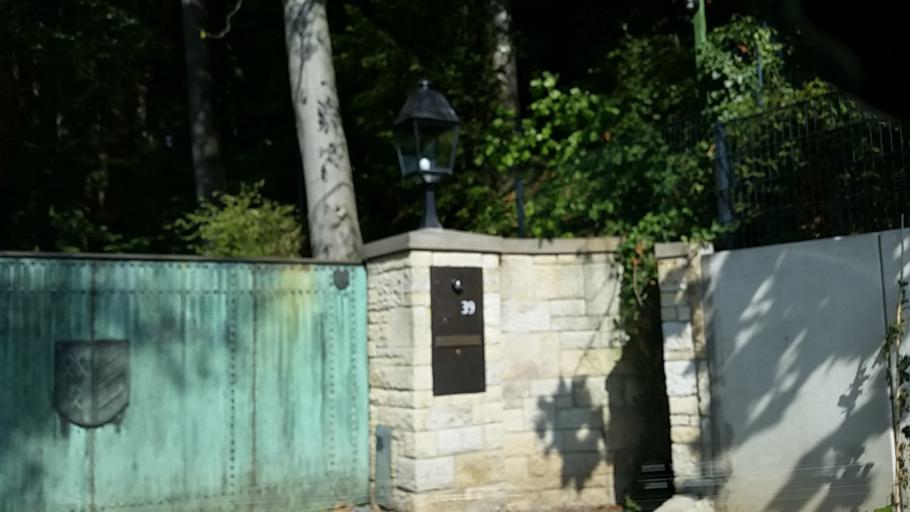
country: DE
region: Schleswig-Holstein
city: Halstenbek
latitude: 53.5536
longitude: 9.8274
